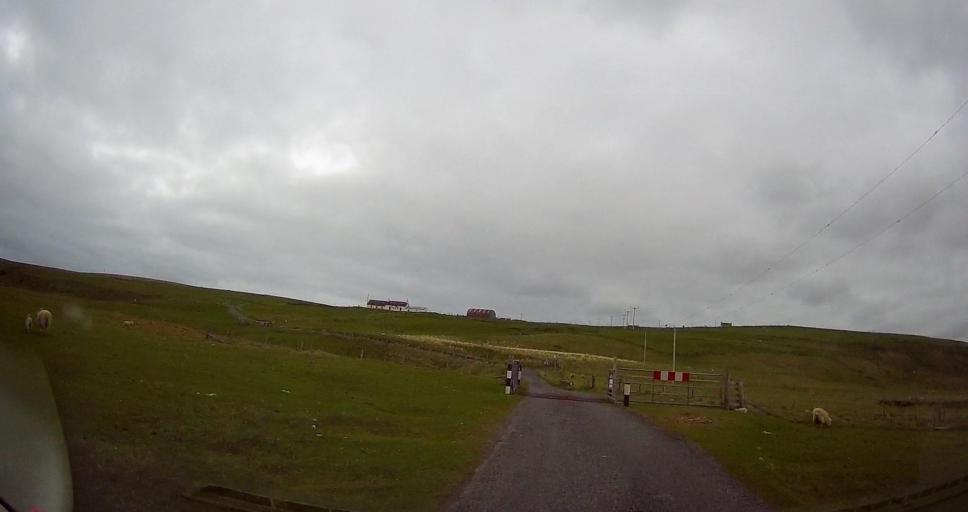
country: GB
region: Scotland
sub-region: Shetland Islands
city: Shetland
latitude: 60.8030
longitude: -0.8833
